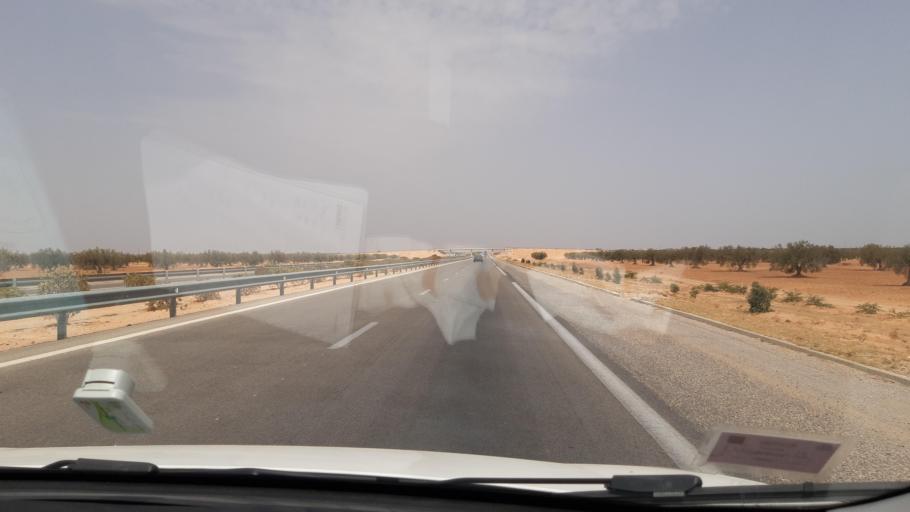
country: TN
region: Safaqis
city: Bi'r `Ali Bin Khalifah
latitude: 34.5727
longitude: 10.3846
